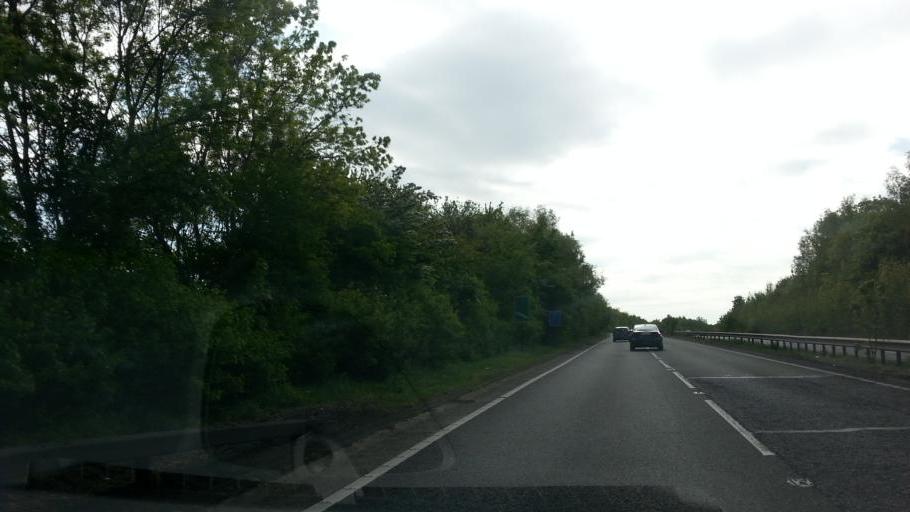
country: GB
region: England
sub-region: Peterborough
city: Castor
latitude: 52.5725
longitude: -0.3158
